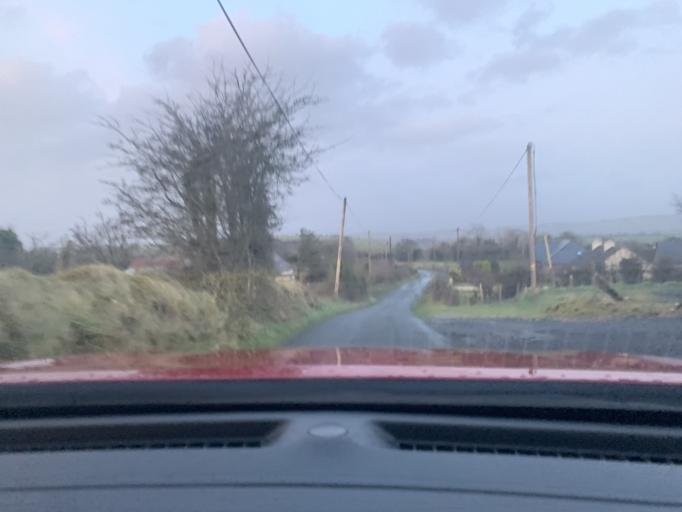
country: IE
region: Connaught
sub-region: Sligo
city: Ballymote
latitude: 54.0756
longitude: -8.3847
